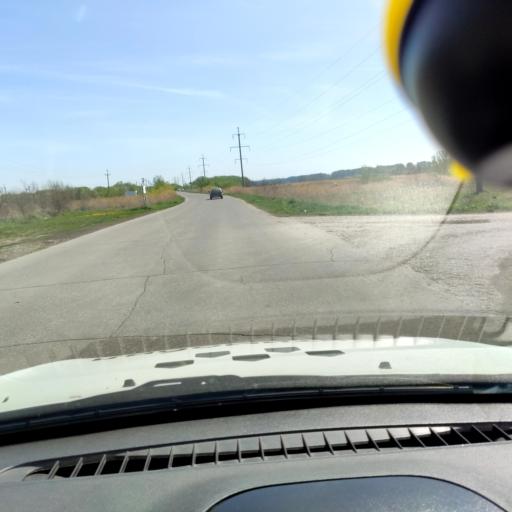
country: RU
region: Samara
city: Tol'yatti
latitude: 53.6636
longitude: 49.3545
